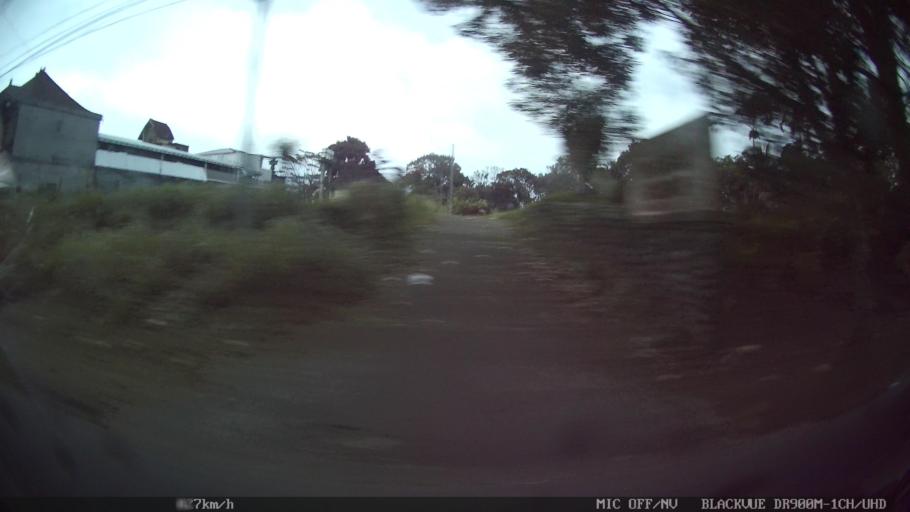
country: ID
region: Bali
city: Banjar Buahan
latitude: -8.4104
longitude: 115.2449
